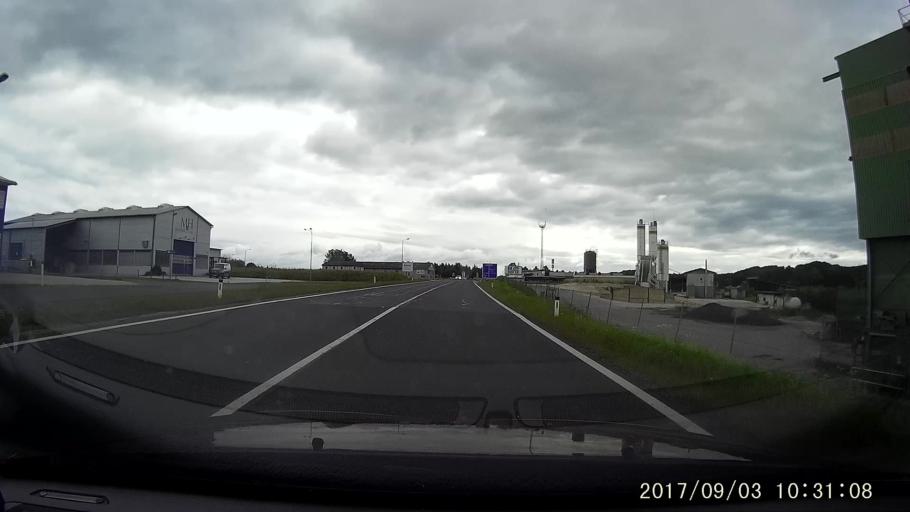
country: AT
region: Styria
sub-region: Politischer Bezirk Hartberg-Fuerstenfeld
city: Ilz
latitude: 47.0826
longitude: 15.9554
